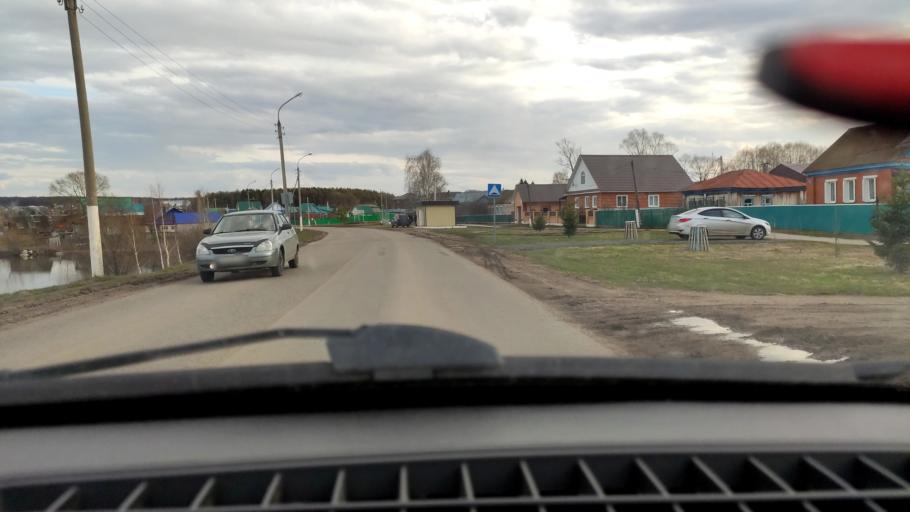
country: RU
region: Bashkortostan
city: Tolbazy
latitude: 54.0303
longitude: 55.8837
